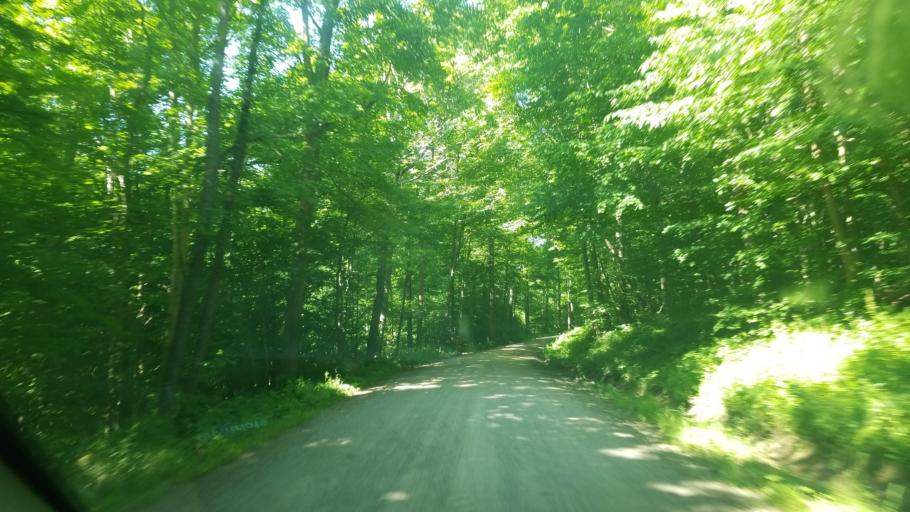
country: US
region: Ohio
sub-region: Holmes County
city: Millersburg
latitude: 40.4335
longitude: -81.9262
